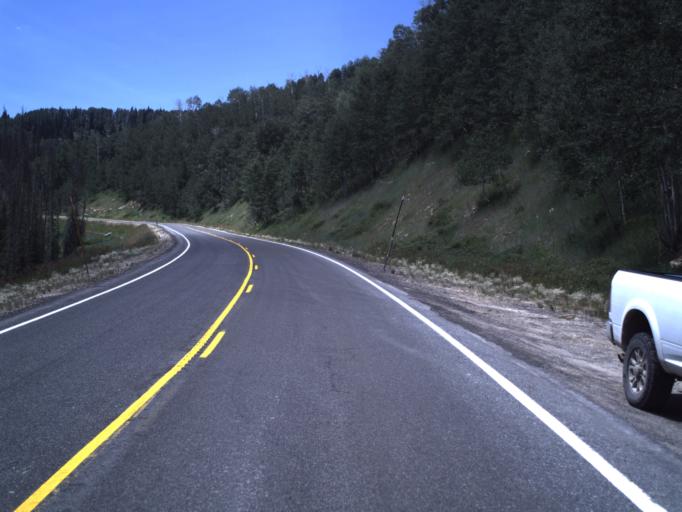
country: US
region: Utah
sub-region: Sanpete County
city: Fairview
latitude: 39.6817
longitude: -111.2082
